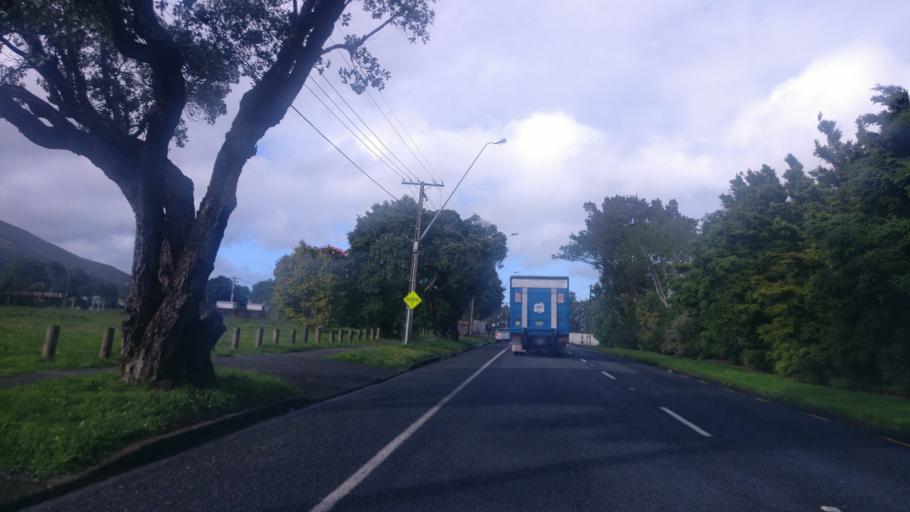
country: NZ
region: Wellington
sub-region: Lower Hutt City
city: Lower Hutt
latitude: -41.2069
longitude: 174.9317
